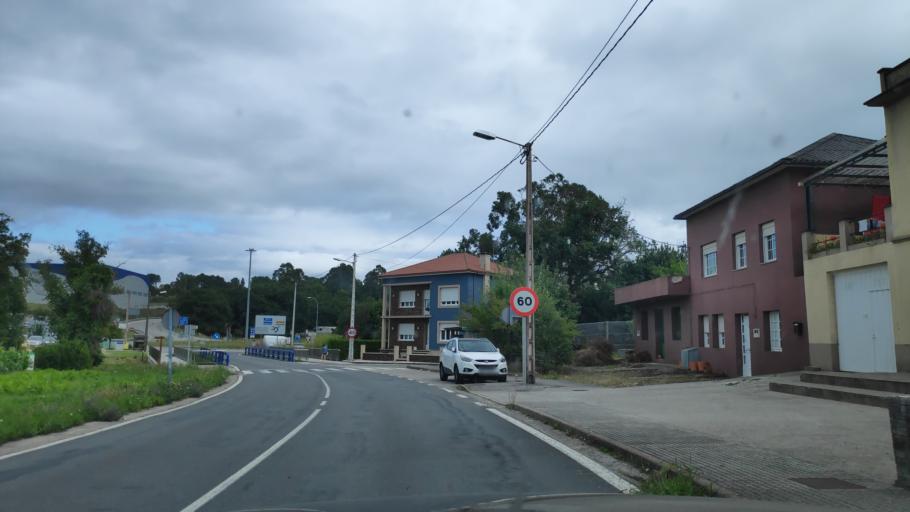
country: ES
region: Galicia
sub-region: Provincia da Coruna
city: Rianxo
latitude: 42.6694
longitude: -8.8135
